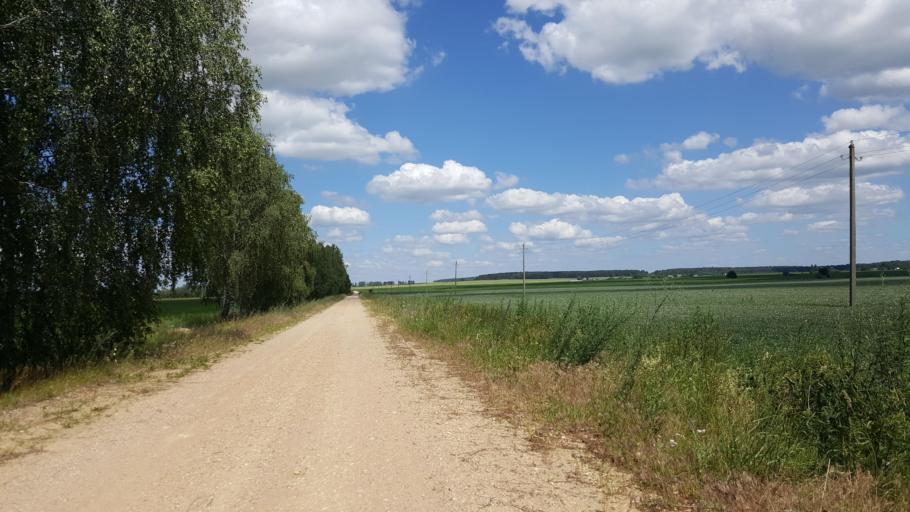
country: BY
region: Brest
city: Vysokaye
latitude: 52.3895
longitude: 23.5435
